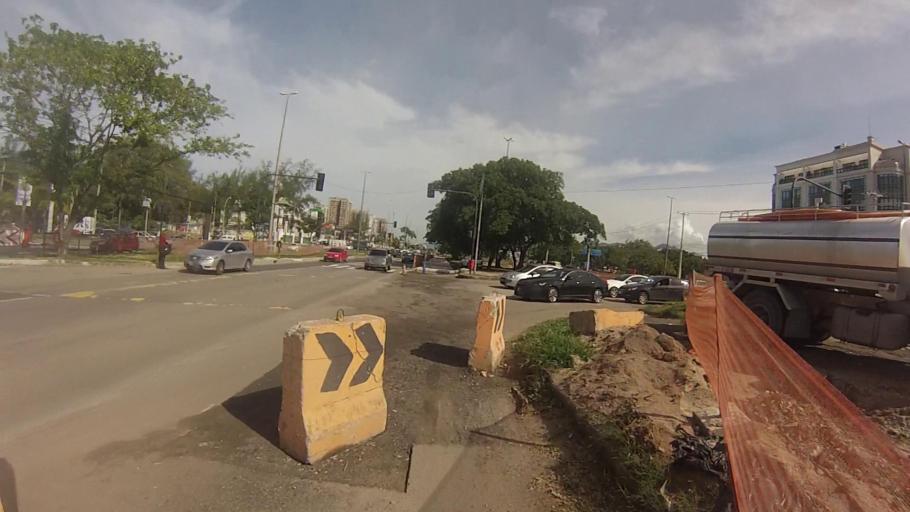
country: BR
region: Rio de Janeiro
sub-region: Rio De Janeiro
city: Rio de Janeiro
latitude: -23.0000
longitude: -43.3533
